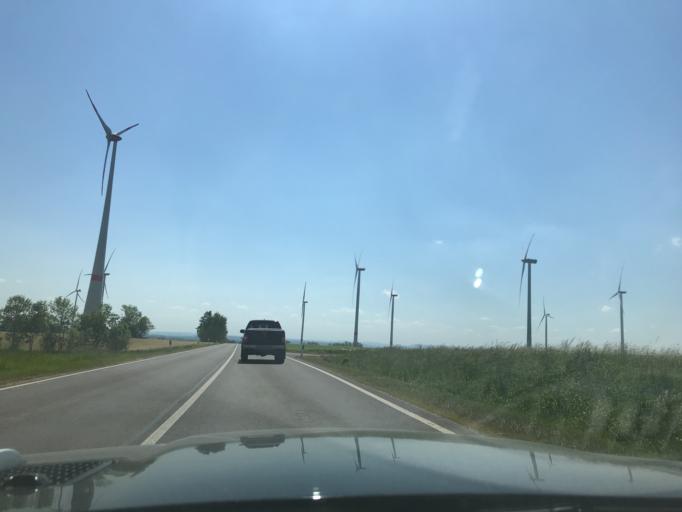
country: DE
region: Thuringia
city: Hochheim
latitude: 51.0411
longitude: 10.6628
